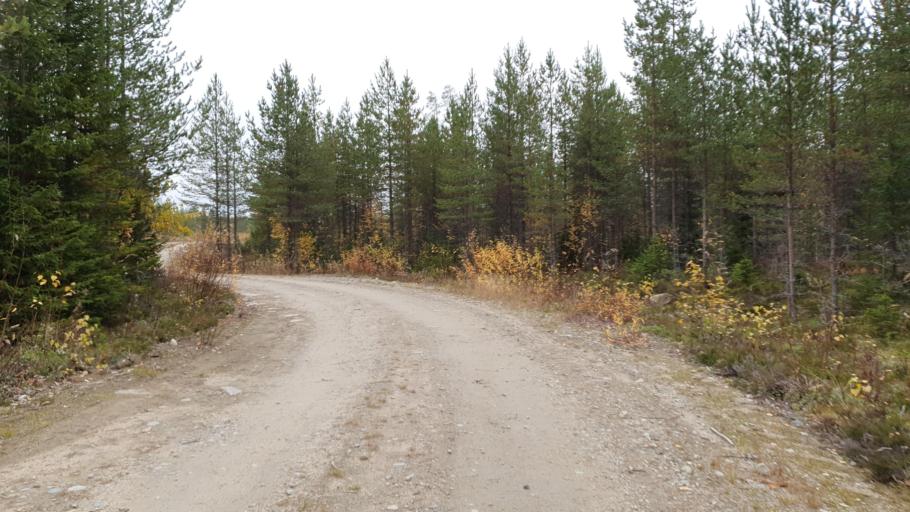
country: FI
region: Kainuu
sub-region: Kehys-Kainuu
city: Kuhmo
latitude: 64.4481
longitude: 29.6160
